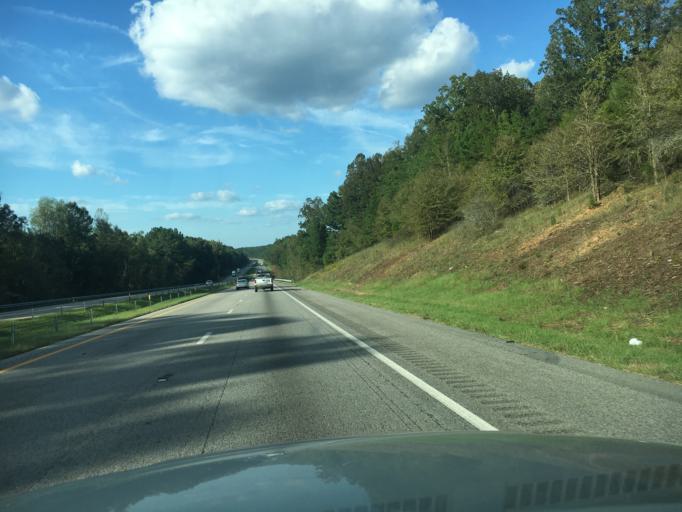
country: US
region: South Carolina
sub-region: Laurens County
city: Clinton
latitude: 34.5826
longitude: -81.8931
